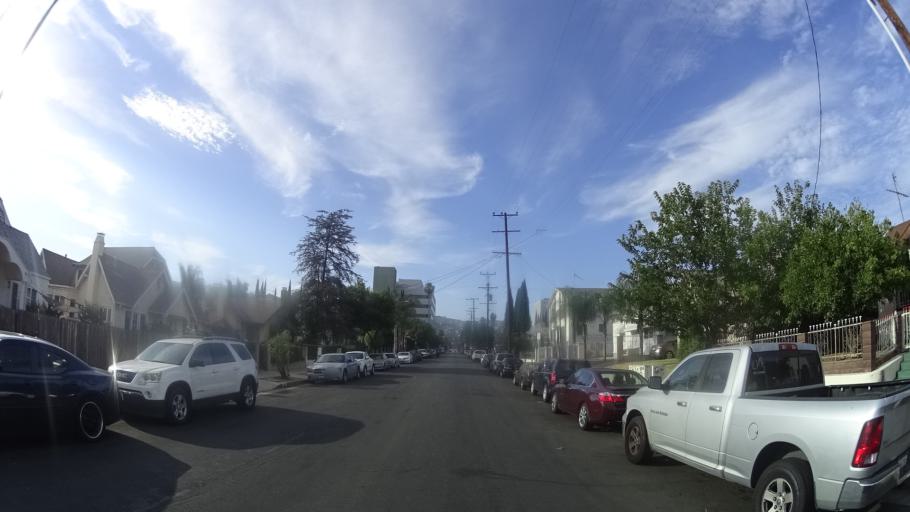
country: US
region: California
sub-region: Los Angeles County
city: Silver Lake
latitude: 34.0960
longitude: -118.2972
